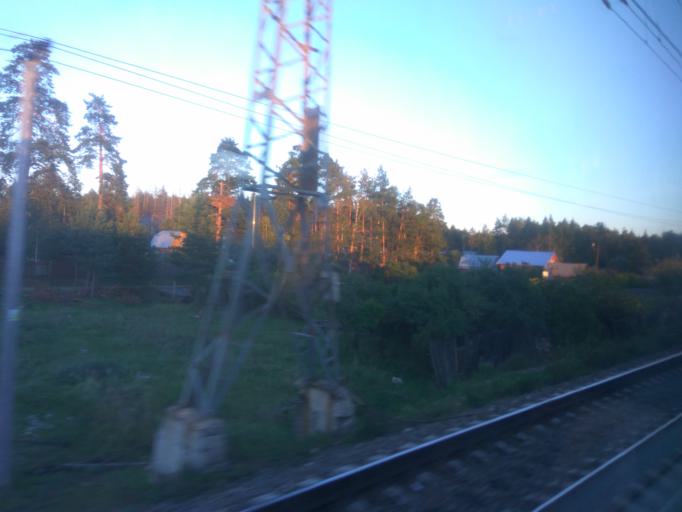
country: RU
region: Moskovskaya
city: Fryazevo
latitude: 55.7463
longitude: 38.4786
